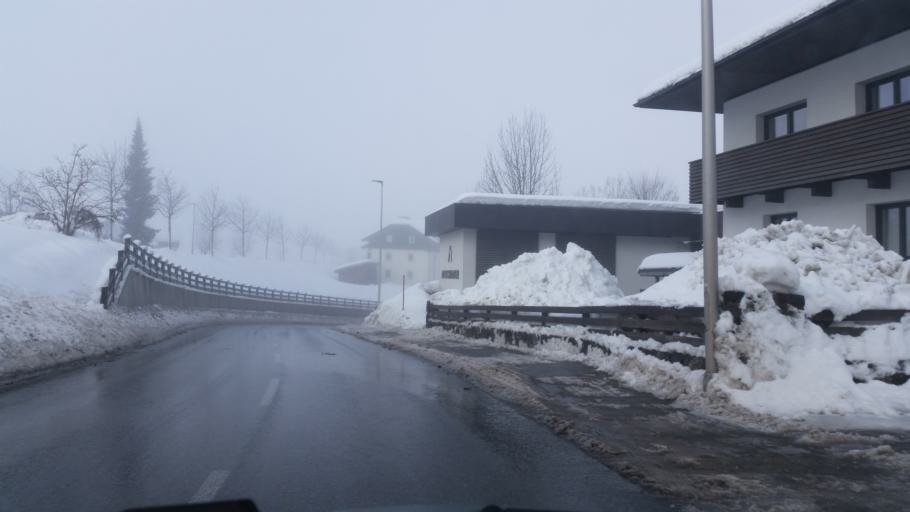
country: AT
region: Tyrol
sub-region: Politischer Bezirk Kitzbuhel
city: Sankt Johann in Tirol
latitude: 47.5191
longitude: 12.4396
